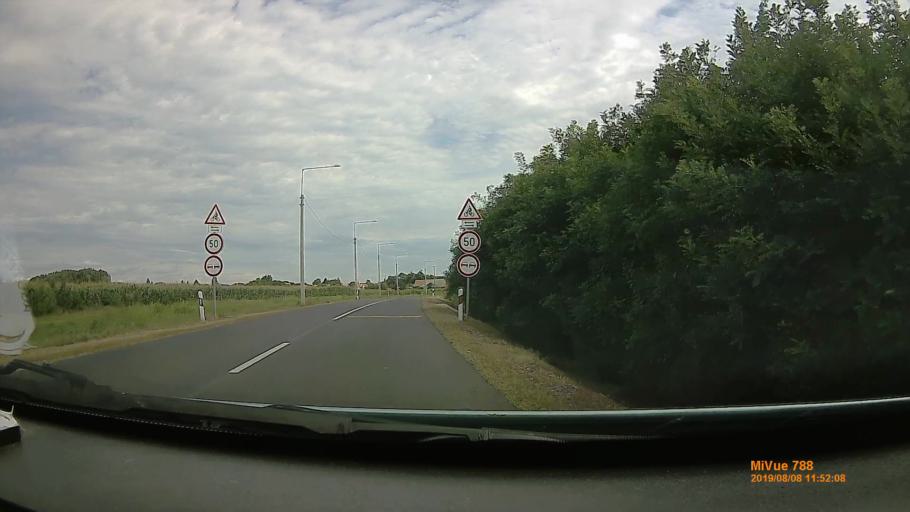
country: HU
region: Szabolcs-Szatmar-Bereg
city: Nyirmihalydi
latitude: 47.7266
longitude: 21.9519
